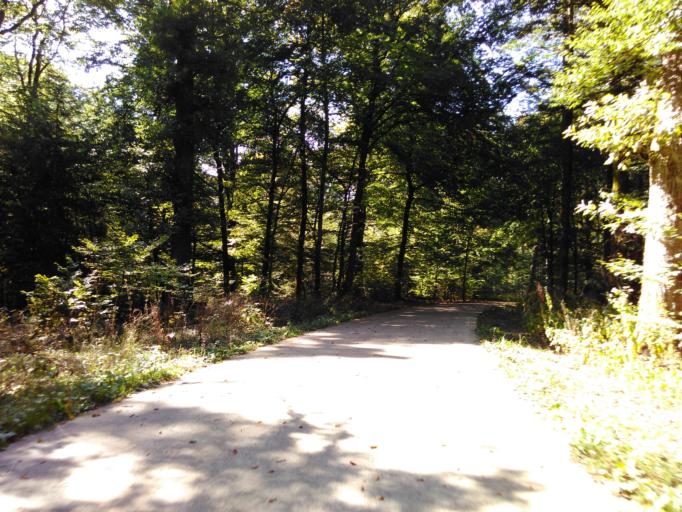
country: LU
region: Diekirch
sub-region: Canton de Redange
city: Rambrouch
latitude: 49.8396
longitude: 5.8074
